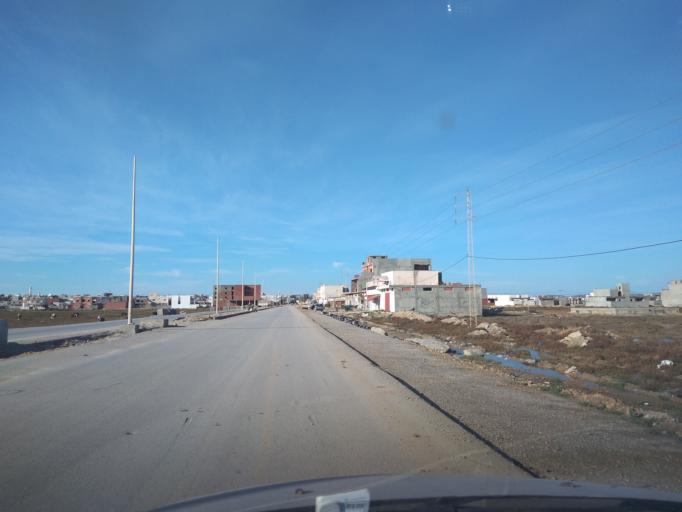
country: TN
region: Ariana
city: Qal'at al Andalus
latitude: 37.0488
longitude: 10.1242
